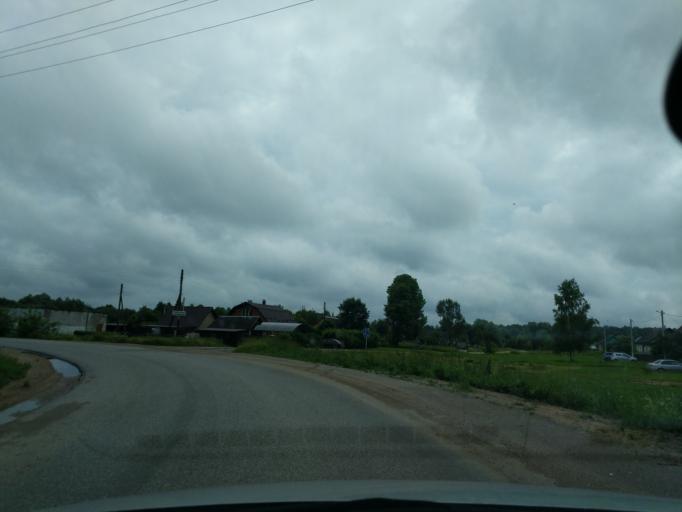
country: RU
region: Kaluga
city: Myatlevo
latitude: 54.8325
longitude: 35.6422
